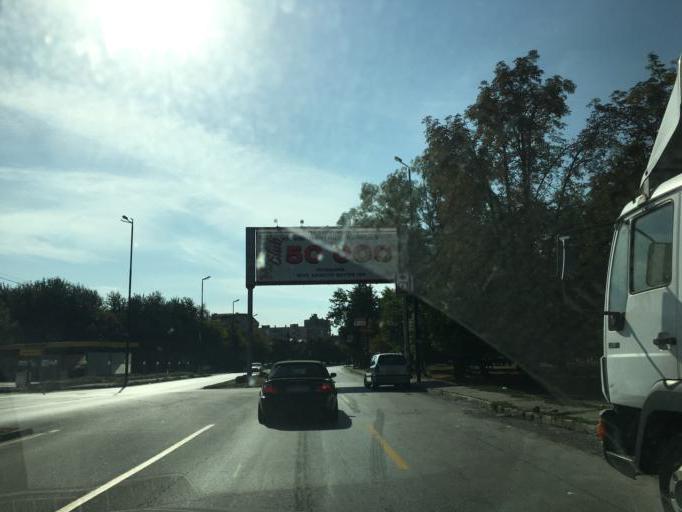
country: BG
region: Pazardzhik
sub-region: Obshtina Pazardzhik
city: Pazardzhik
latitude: 42.2079
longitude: 24.3273
